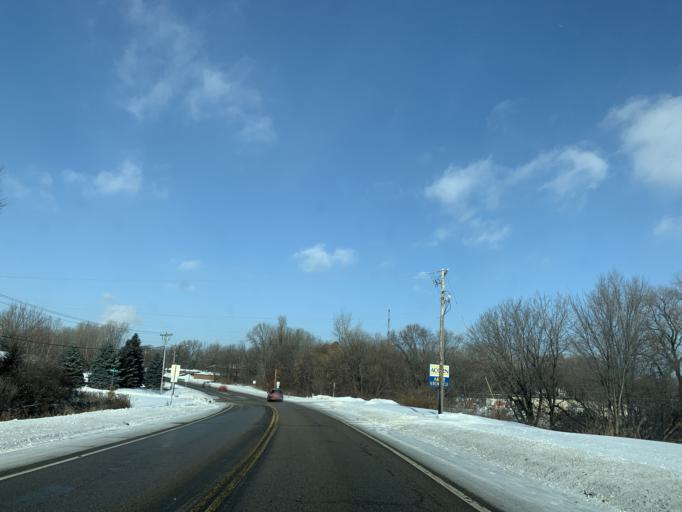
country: US
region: Minnesota
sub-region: Dakota County
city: South Saint Paul
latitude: 44.8760
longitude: -93.0646
